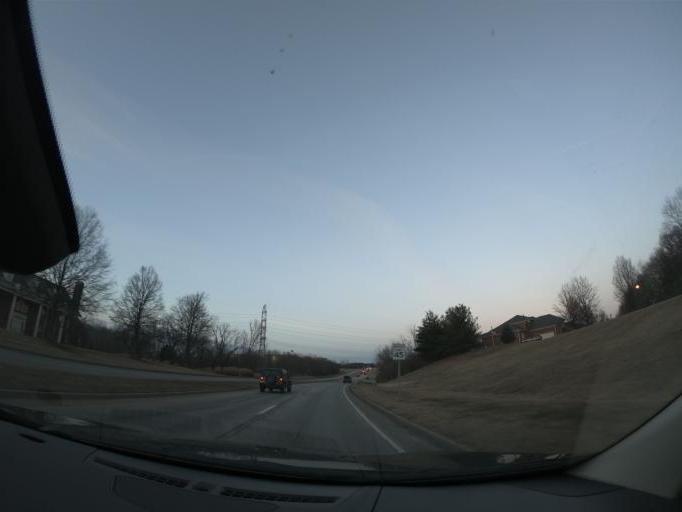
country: US
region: Kentucky
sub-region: Jefferson County
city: Hurstbourne
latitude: 38.2592
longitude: -85.5785
